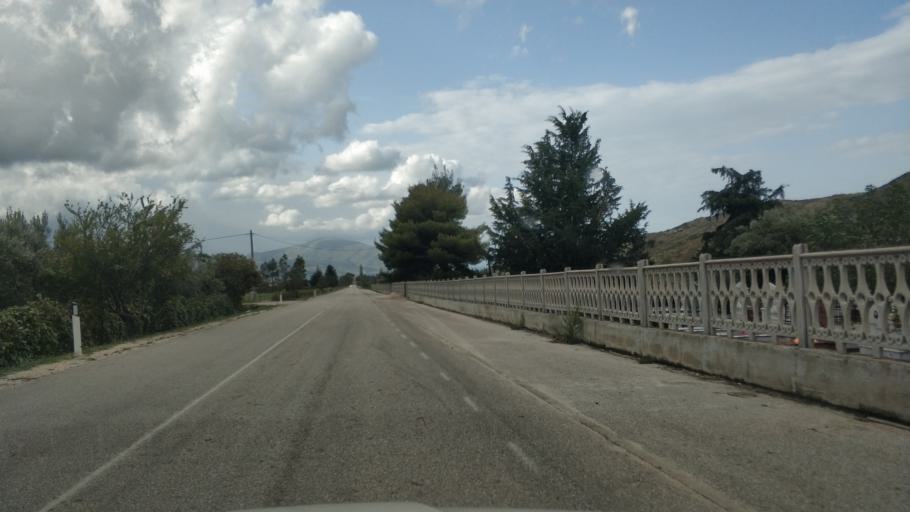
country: AL
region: Vlore
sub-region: Rrethi i Vlores
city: Orikum
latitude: 40.2722
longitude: 19.5120
